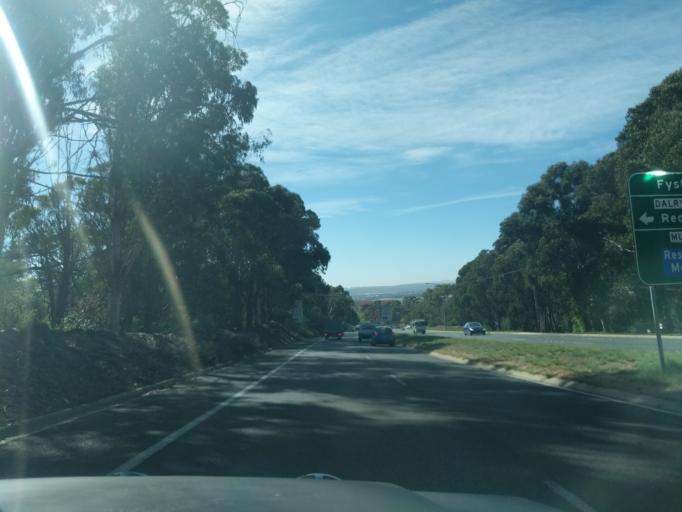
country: AU
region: Australian Capital Territory
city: Forrest
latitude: -35.3443
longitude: 149.1340
